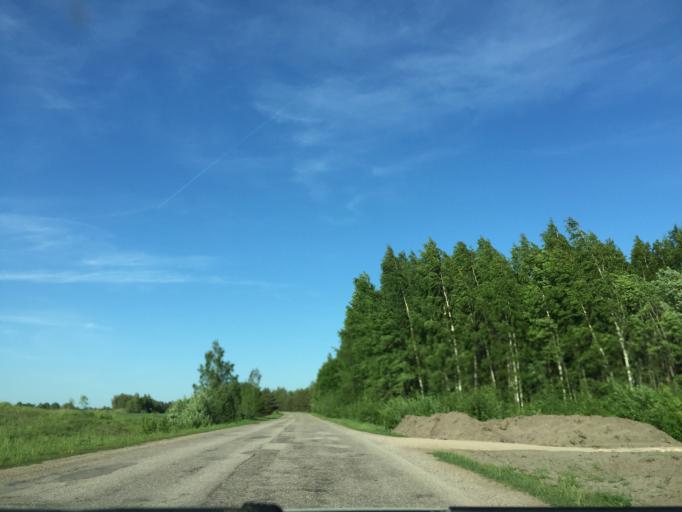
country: LV
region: Jelgava
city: Jelgava
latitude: 56.5492
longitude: 23.6371
